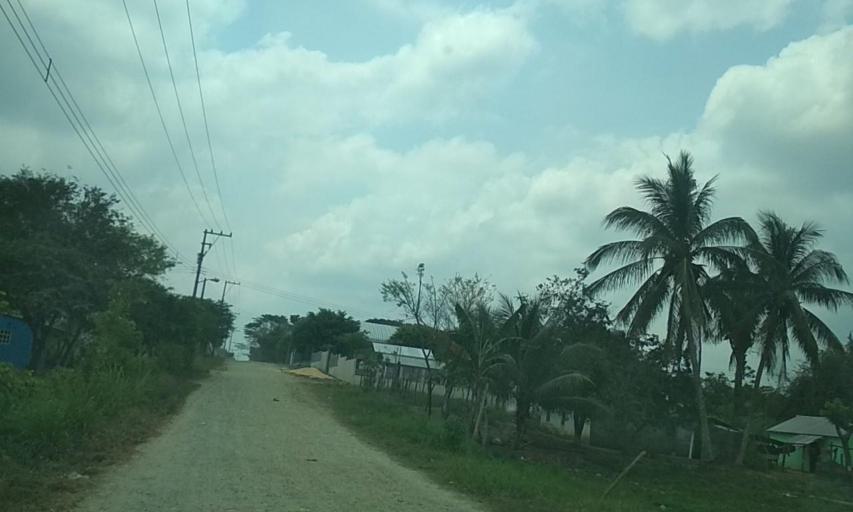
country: MX
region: Tabasco
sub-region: Huimanguillo
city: Francisco Rueda
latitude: 17.6020
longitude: -93.7970
